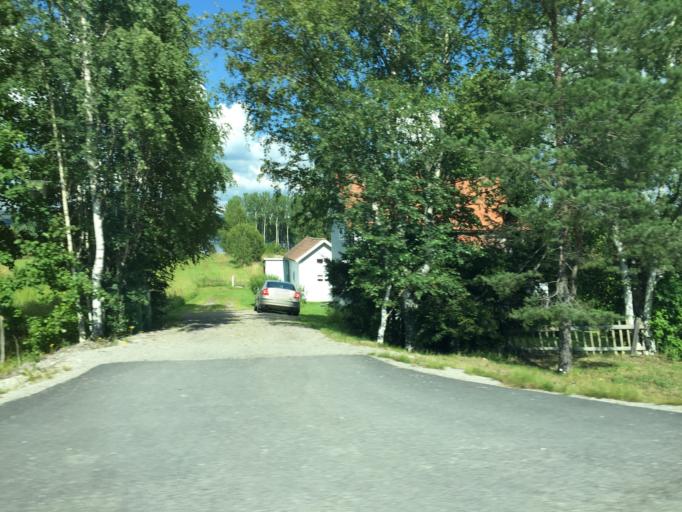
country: SE
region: Gaevleborg
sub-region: Bollnas Kommun
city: Bollnas
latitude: 61.3104
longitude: 16.4508
